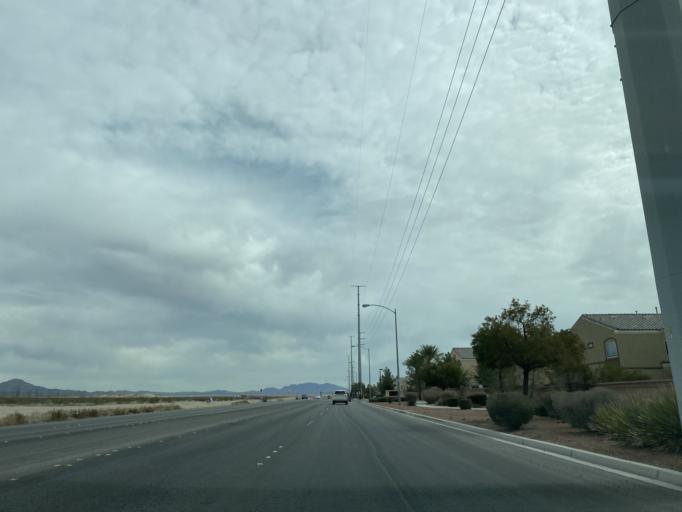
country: US
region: Nevada
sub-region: Clark County
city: Nellis Air Force Base
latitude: 36.2765
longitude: -115.0884
